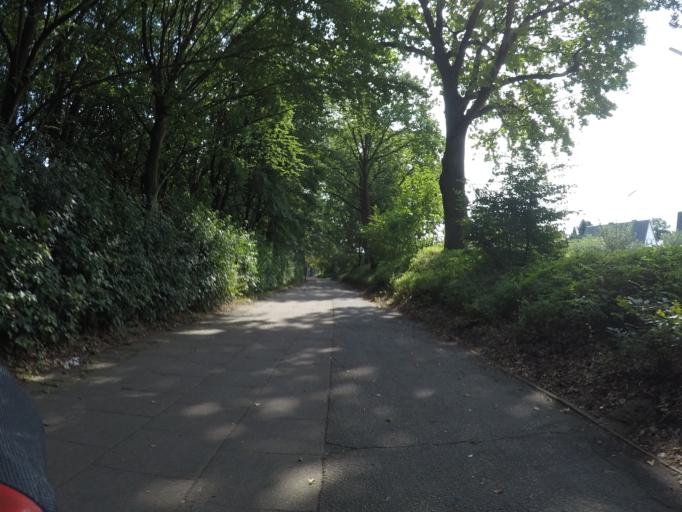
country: DE
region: Hamburg
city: Poppenbuettel
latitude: 53.6643
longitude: 10.0747
